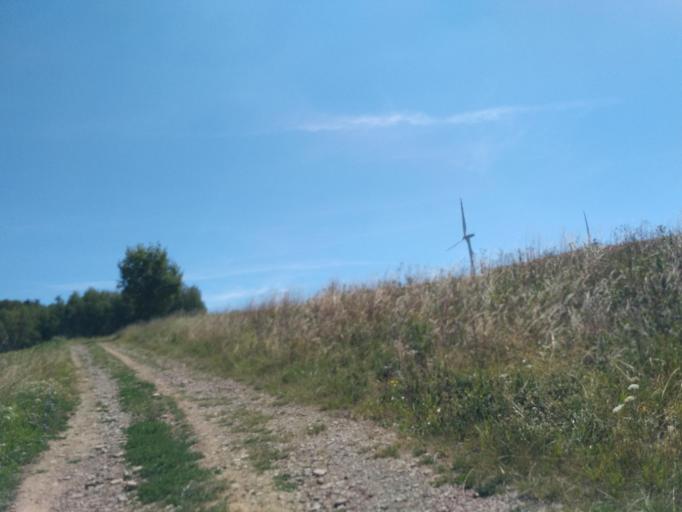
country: PL
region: Subcarpathian Voivodeship
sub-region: Powiat sanocki
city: Bukowsko
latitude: 49.5146
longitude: 22.0485
